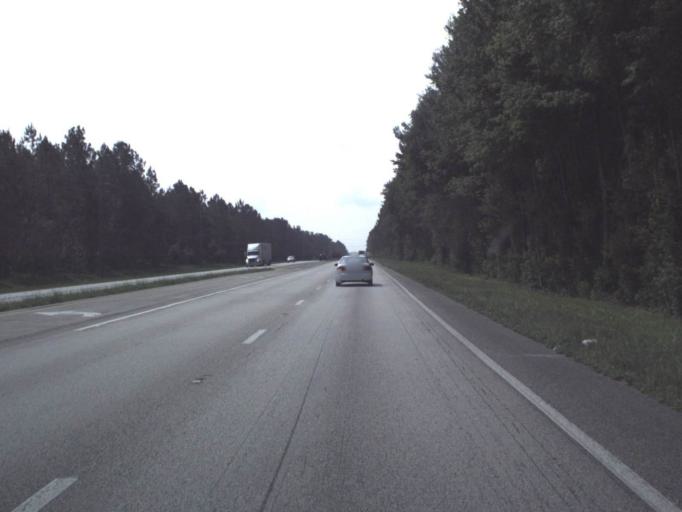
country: US
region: Florida
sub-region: Nassau County
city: Nassau Village-Ratliff
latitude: 30.4660
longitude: -81.7769
